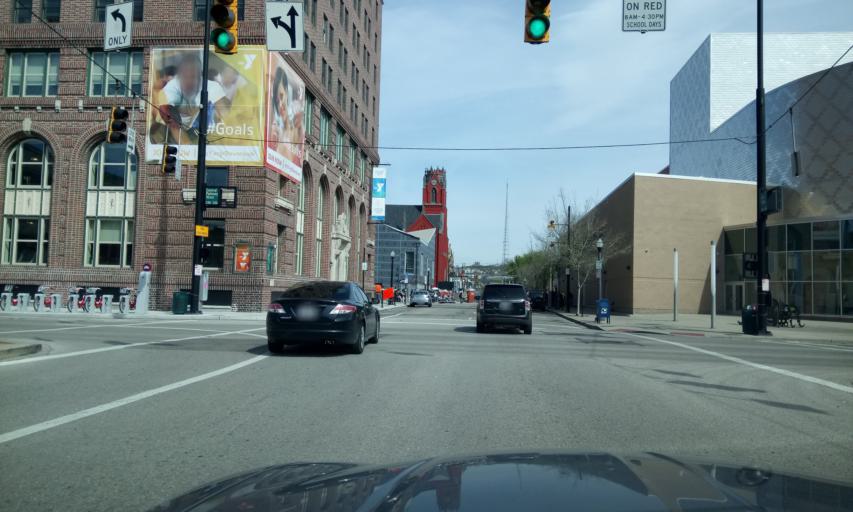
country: US
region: Kentucky
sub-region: Kenton County
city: Covington
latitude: 39.1064
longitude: -84.5177
